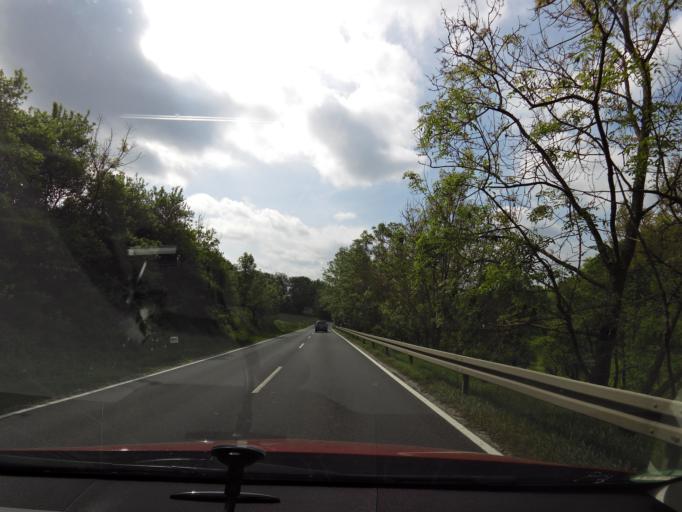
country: DE
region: Thuringia
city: Nazza
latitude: 51.0932
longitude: 10.3289
